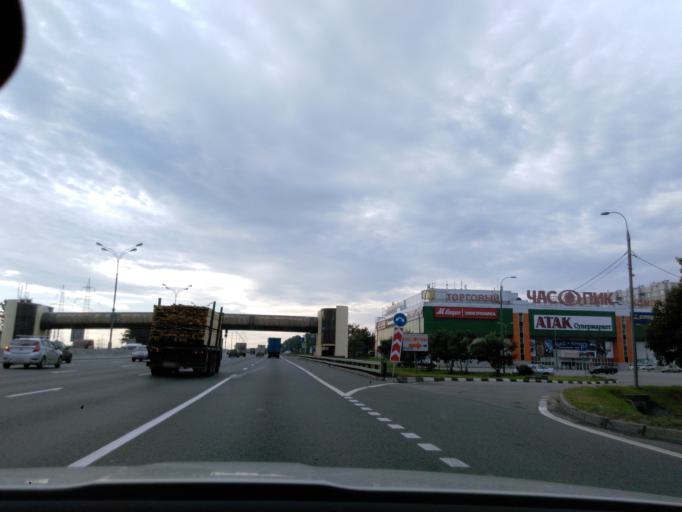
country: RU
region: Moscow
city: Bibirevo
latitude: 55.9000
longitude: 37.6265
